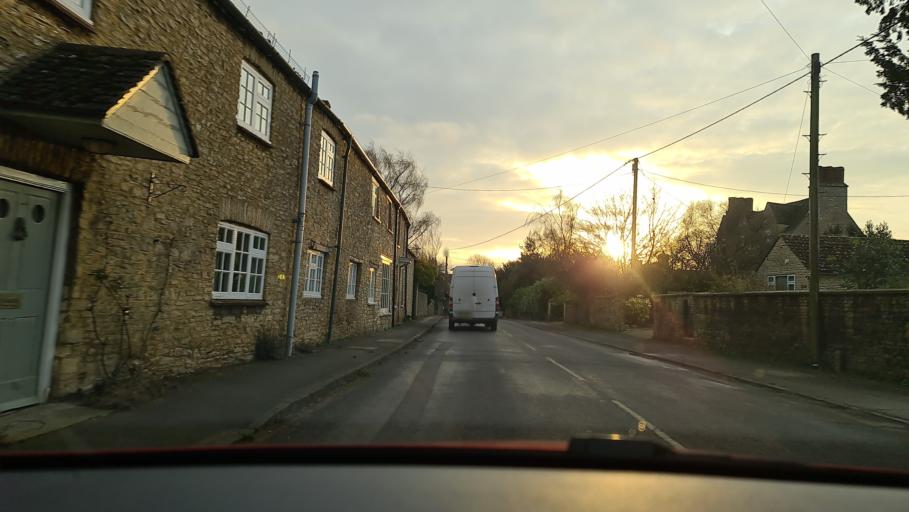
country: GB
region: England
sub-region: Oxfordshire
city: Kidlington
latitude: 51.8546
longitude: -1.2717
